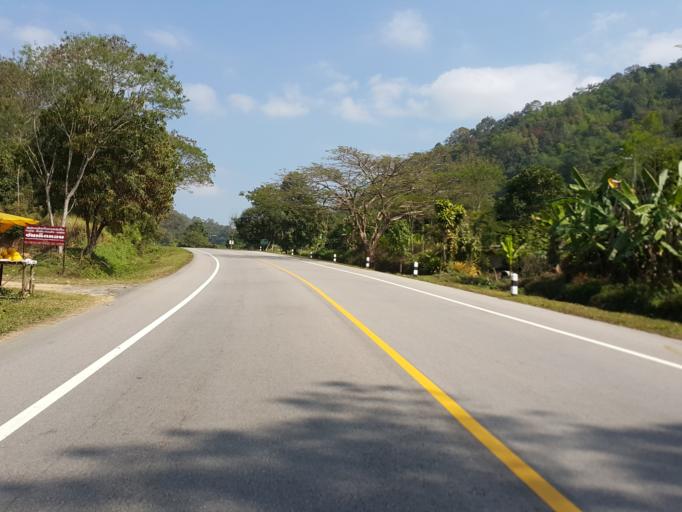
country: TH
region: Chiang Mai
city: Mae On
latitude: 19.0424
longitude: 99.3390
